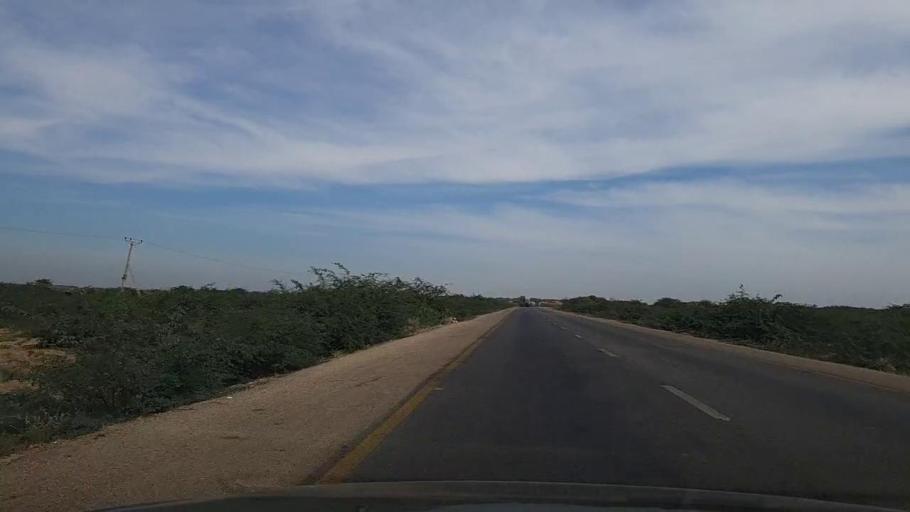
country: PK
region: Sindh
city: Thatta
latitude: 24.8433
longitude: 68.0082
